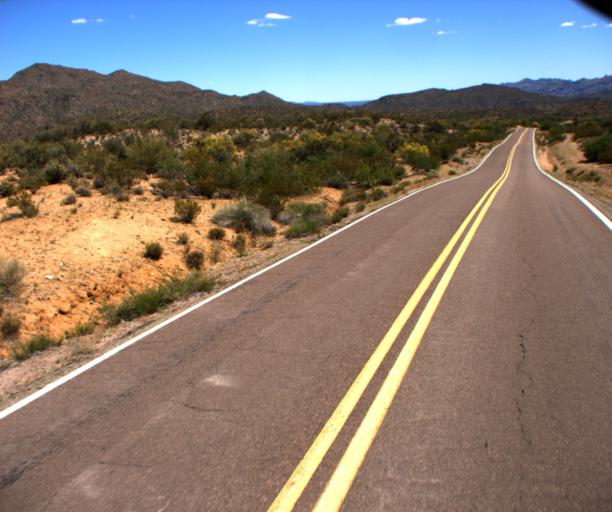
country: US
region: Arizona
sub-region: Yavapai County
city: Bagdad
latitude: 34.4574
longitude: -113.2432
